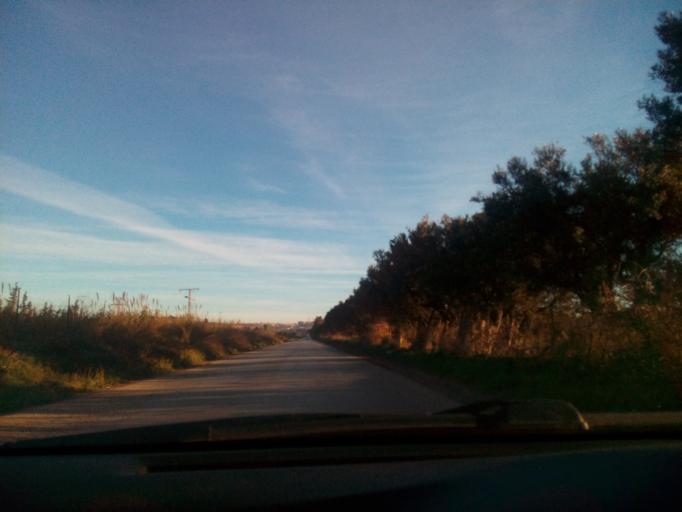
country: DZ
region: Oran
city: Es Senia
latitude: 35.6142
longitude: -0.6865
